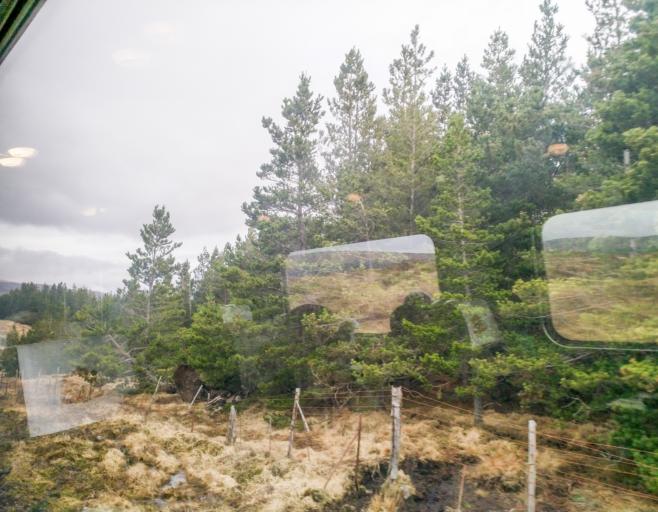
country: GB
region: Scotland
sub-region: Highland
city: Spean Bridge
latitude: 56.6592
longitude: -4.5645
